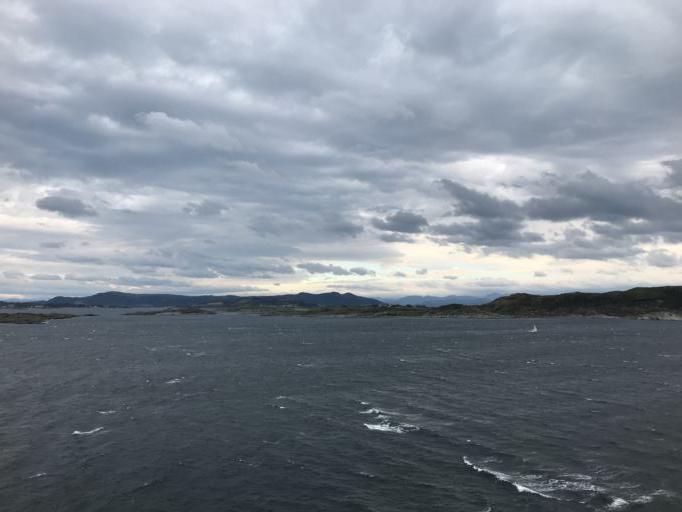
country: NO
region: Rogaland
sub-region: Randaberg
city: Randaberg
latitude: 59.0421
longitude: 5.6049
